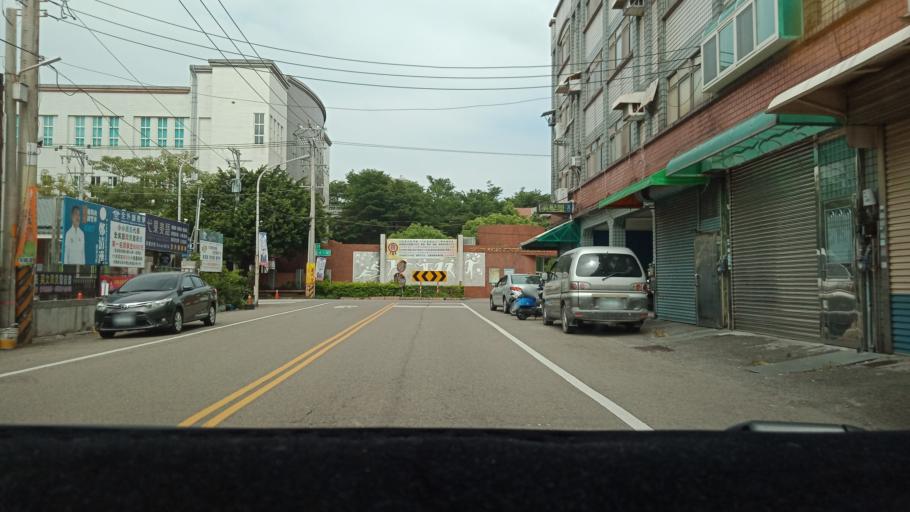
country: TW
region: Taiwan
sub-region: Hsinchu
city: Zhubei
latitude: 24.8788
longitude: 120.9992
